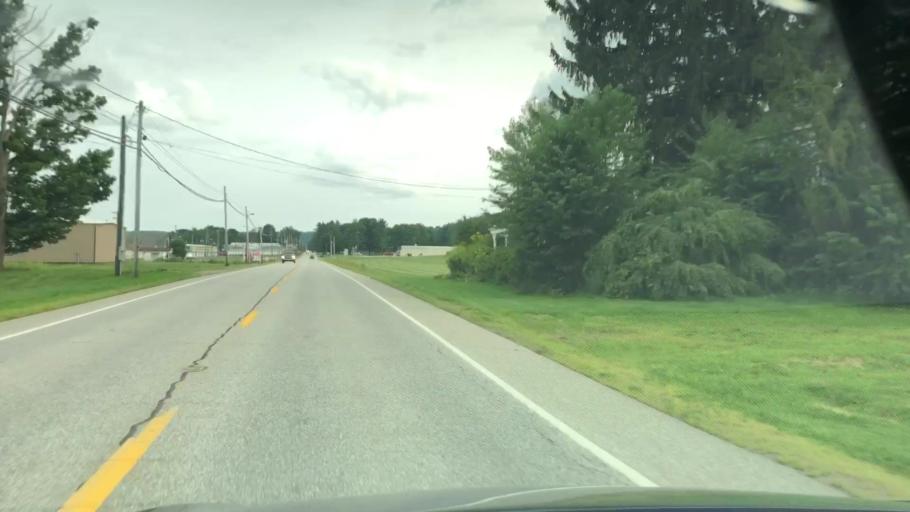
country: US
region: Pennsylvania
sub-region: Erie County
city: Union City
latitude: 42.0177
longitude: -79.8167
